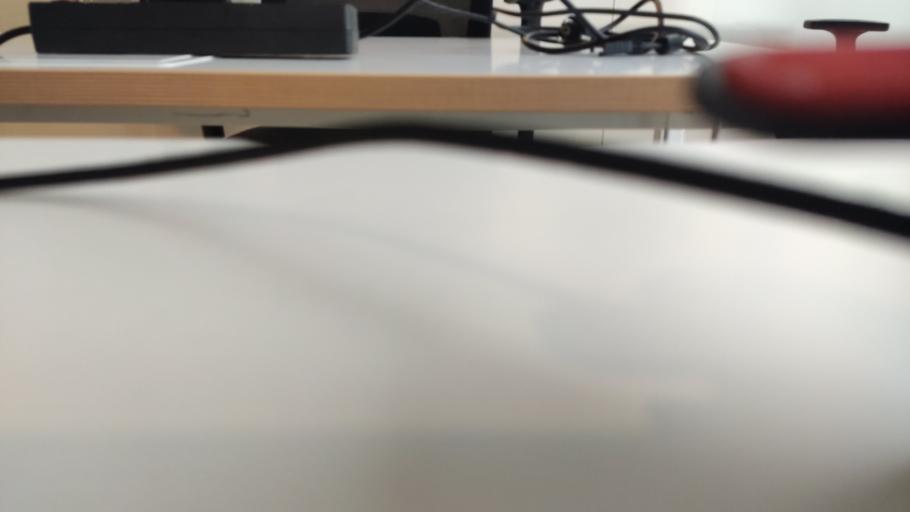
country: RU
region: Moskovskaya
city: Rogachevo
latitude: 56.4266
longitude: 37.1032
